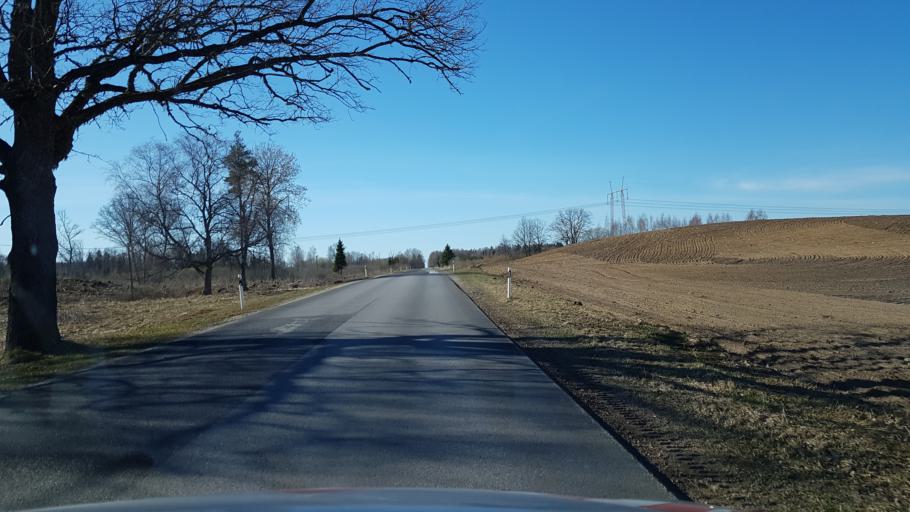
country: EE
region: Laeaene-Virumaa
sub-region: Vinni vald
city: Vinni
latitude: 59.3101
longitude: 26.5253
